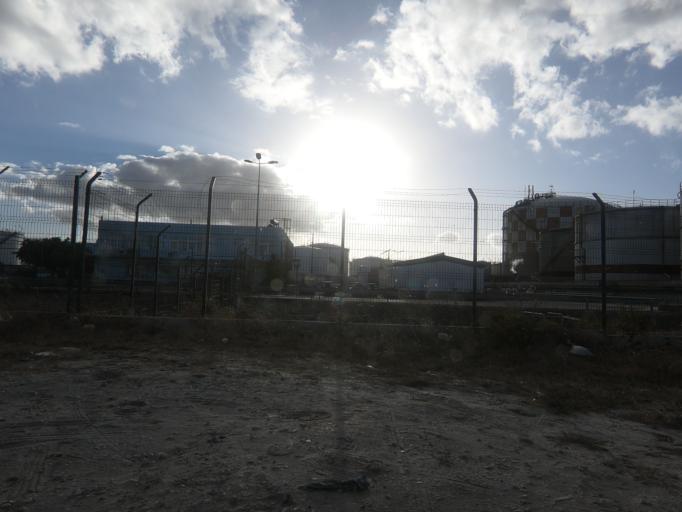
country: PT
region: Setubal
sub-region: Barreiro
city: Barreiro
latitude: 38.6820
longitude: -9.0570
